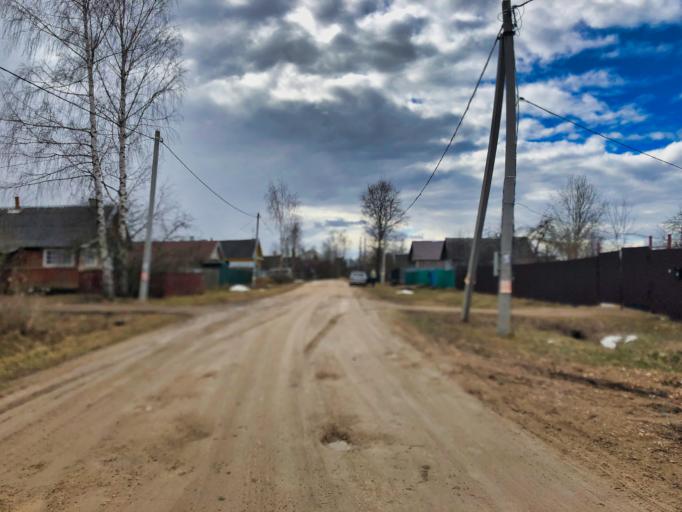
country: RU
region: Tverskaya
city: Rzhev
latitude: 56.2270
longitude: 34.3088
